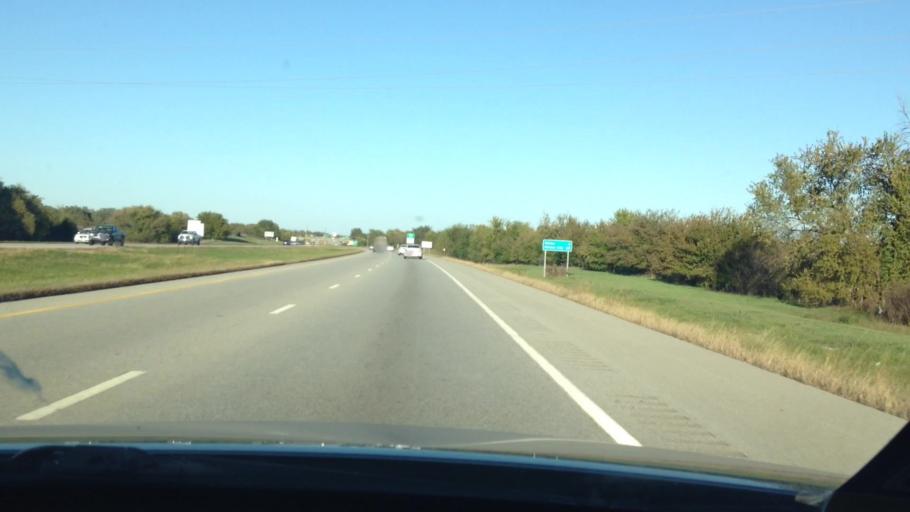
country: US
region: Kansas
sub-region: Johnson County
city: Gardner
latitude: 38.8187
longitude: -94.8679
